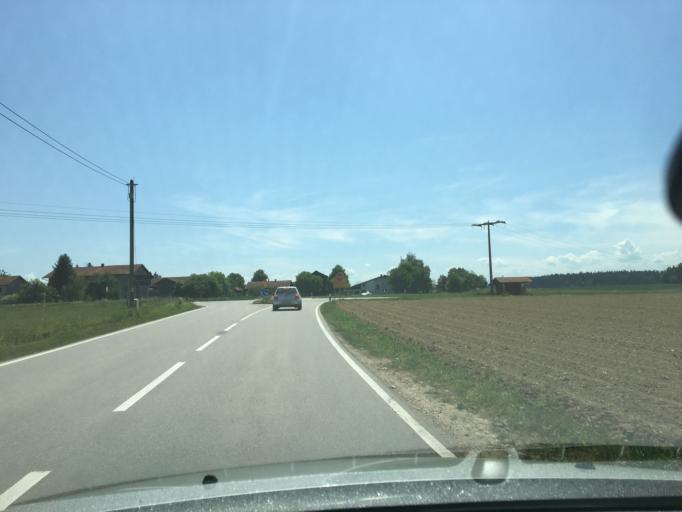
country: DE
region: Bavaria
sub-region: Upper Bavaria
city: Halsbach
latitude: 48.1113
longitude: 12.6834
